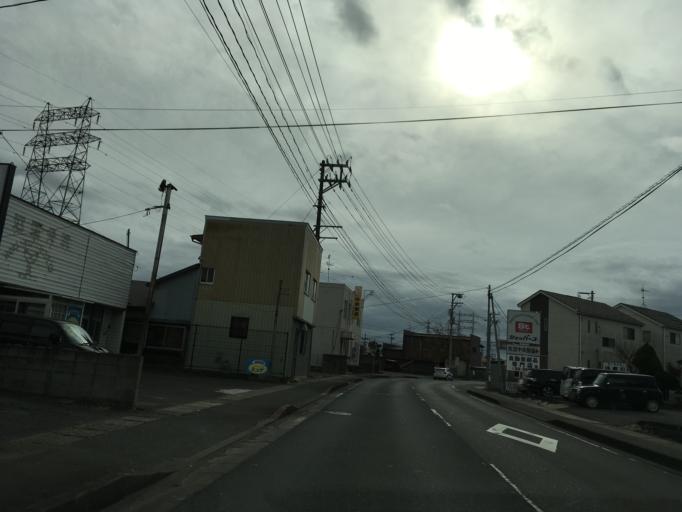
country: JP
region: Miyagi
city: Wakuya
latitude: 38.6915
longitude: 141.2063
